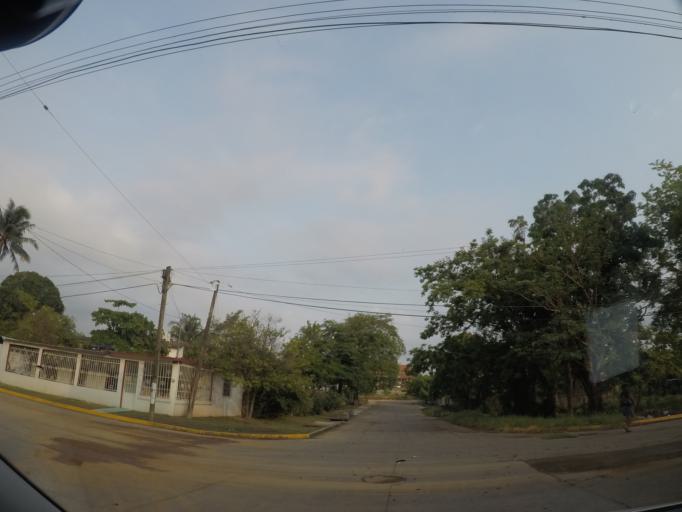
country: MX
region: Oaxaca
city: Matias Romero
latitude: 16.8723
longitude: -95.0442
